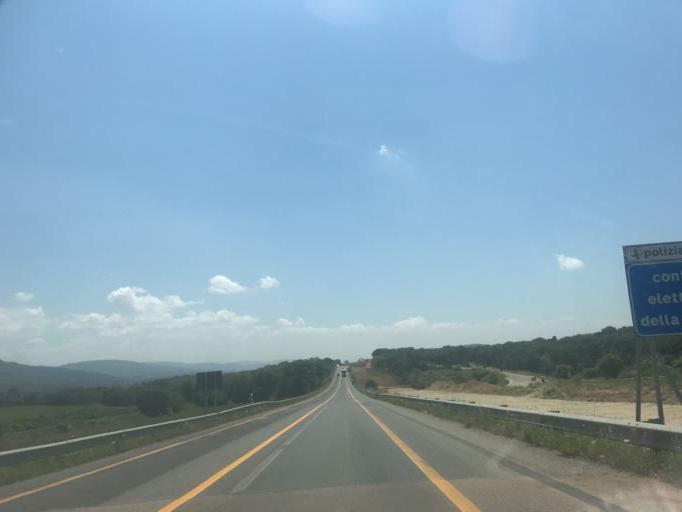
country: IT
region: Sardinia
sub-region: Provincia di Olbia-Tempio
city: Monti
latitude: 40.7972
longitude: 9.2721
